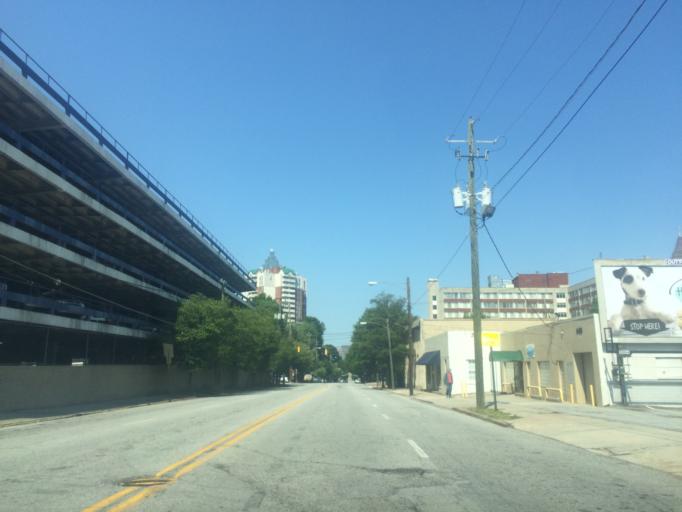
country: US
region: Georgia
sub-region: Fulton County
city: Atlanta
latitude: 33.7640
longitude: -84.3725
